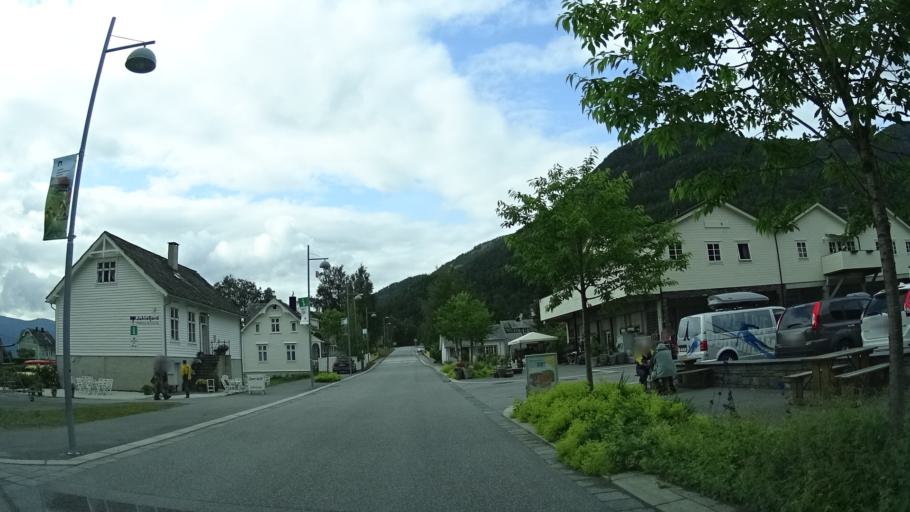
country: NO
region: Hordaland
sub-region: Jondal
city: Jondal
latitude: 60.2768
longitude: 6.2519
